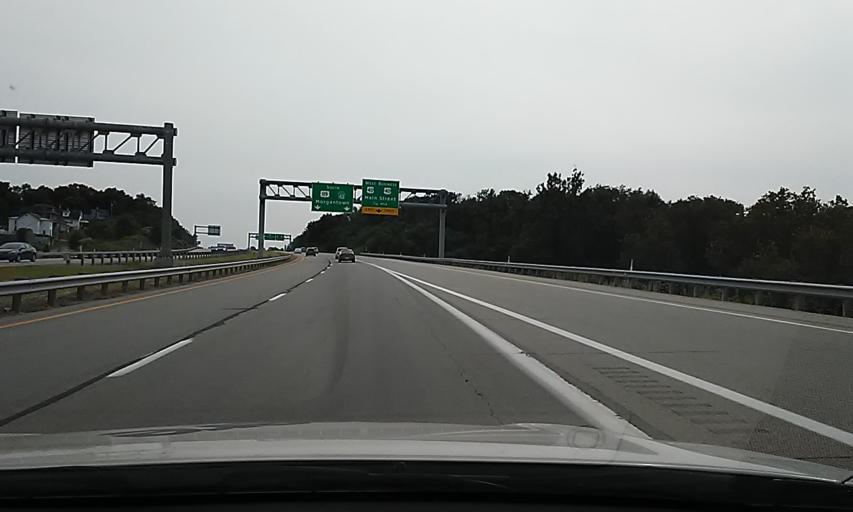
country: US
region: Pennsylvania
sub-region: Fayette County
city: Oliver
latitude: 39.9131
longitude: -79.7341
